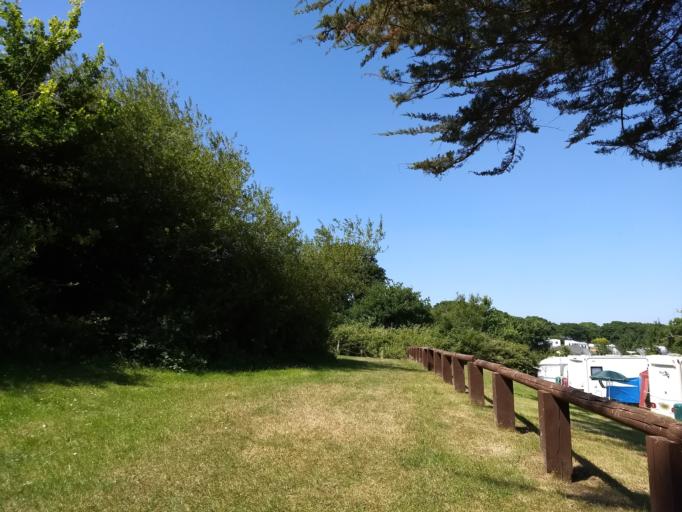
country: GB
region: England
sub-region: Isle of Wight
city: Gurnard
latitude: 50.7316
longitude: -1.3622
